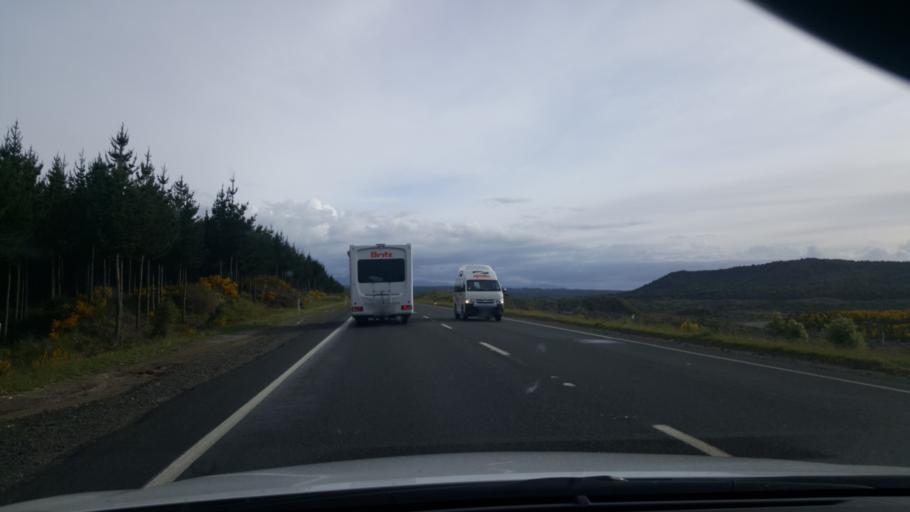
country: NZ
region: Waikato
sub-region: Taupo District
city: Taupo
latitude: -38.8306
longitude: 176.0660
